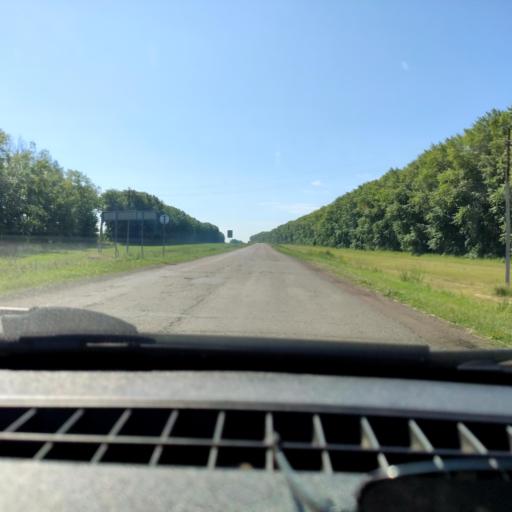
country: RU
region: Bashkortostan
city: Karmaskaly
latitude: 54.3983
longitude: 56.1679
